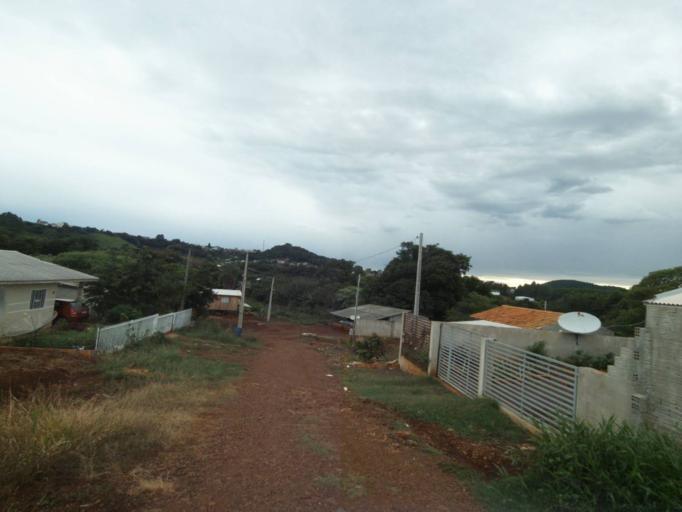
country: BR
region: Parana
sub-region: Guaraniacu
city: Guaraniacu
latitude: -25.1004
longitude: -52.8850
